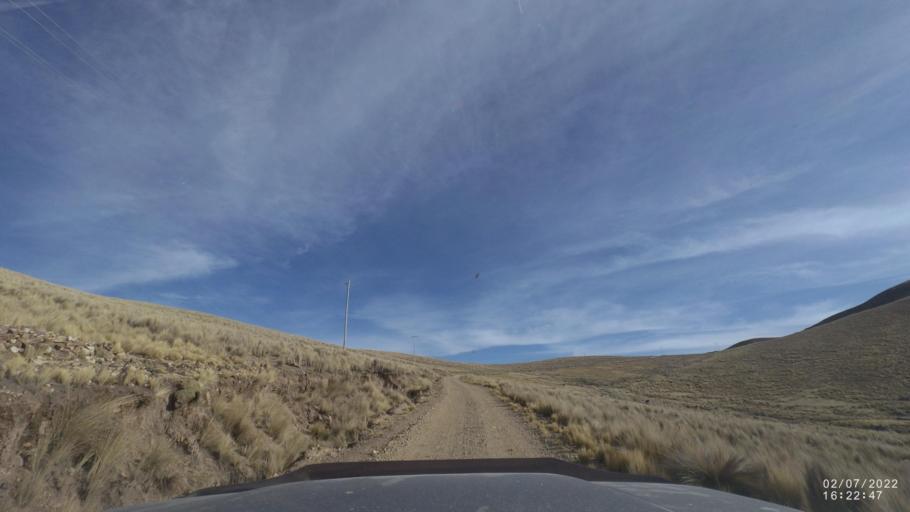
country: BO
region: Cochabamba
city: Irpa Irpa
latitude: -17.9367
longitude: -66.4565
